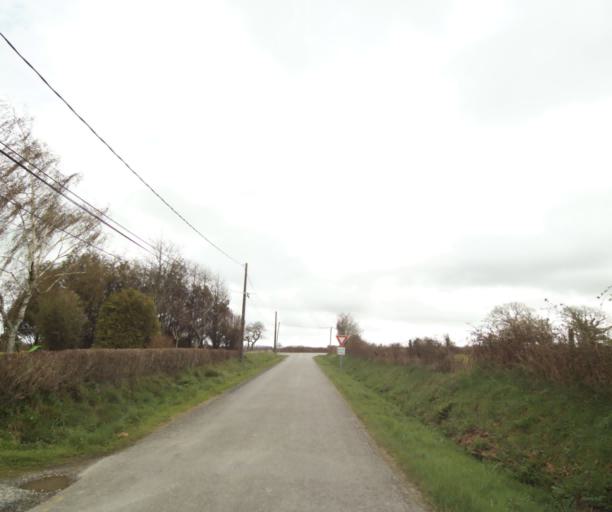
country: FR
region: Pays de la Loire
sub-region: Departement de la Loire-Atlantique
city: Bouvron
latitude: 47.4291
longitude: -1.8544
